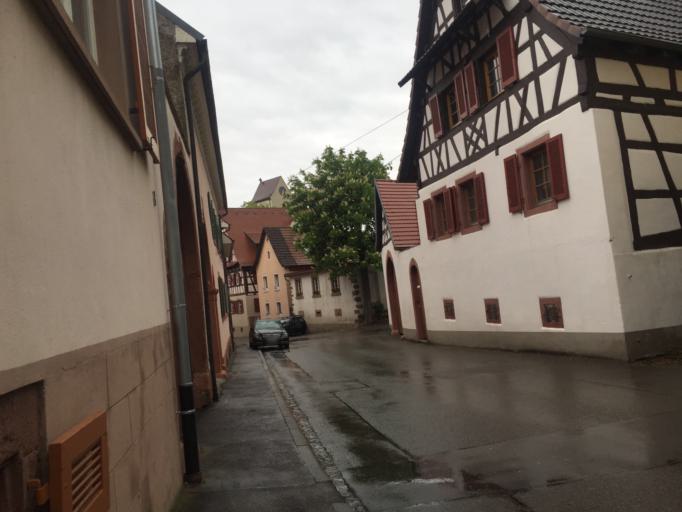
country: DE
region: Baden-Wuerttemberg
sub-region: Freiburg Region
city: Vogtsburg
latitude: 48.1043
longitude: 7.6292
